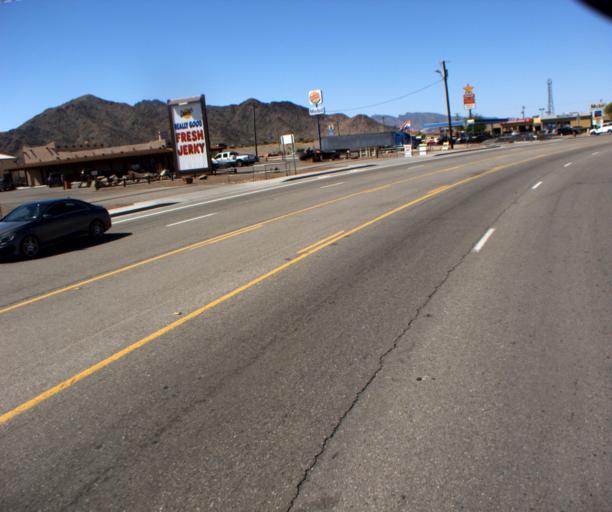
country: US
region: Arizona
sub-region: La Paz County
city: Quartzsite
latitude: 33.6617
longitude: -114.2388
